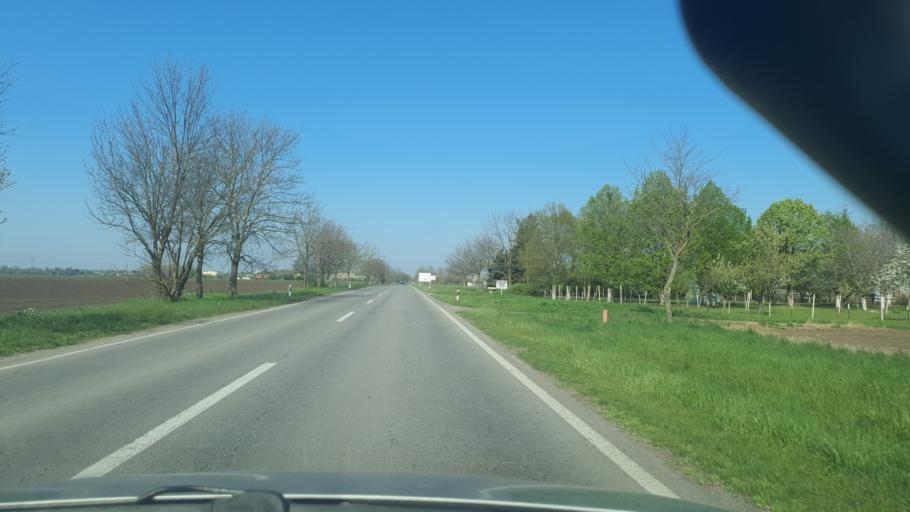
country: RS
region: Autonomna Pokrajina Vojvodina
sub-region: Zapadnobacki Okrug
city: Sombor
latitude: 45.7685
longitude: 19.1637
